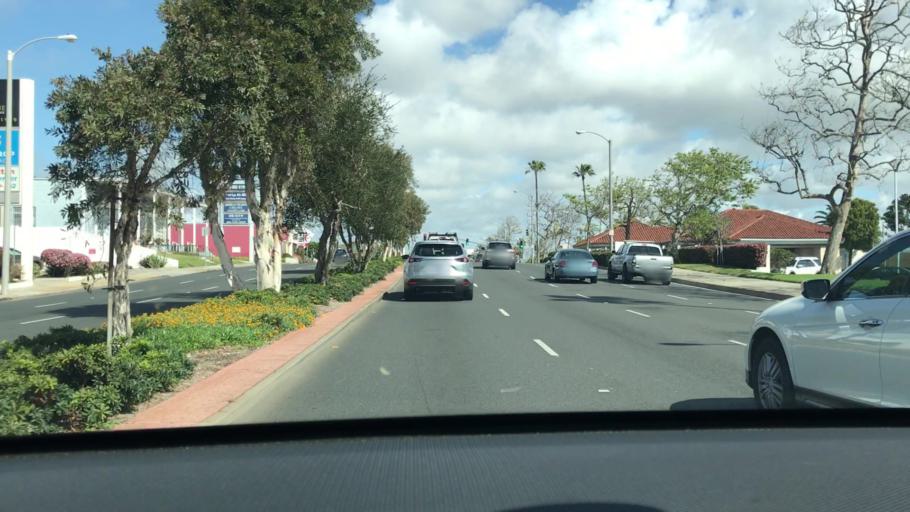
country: US
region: California
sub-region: Los Angeles County
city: Manhattan Beach
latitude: 33.8959
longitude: -118.3960
